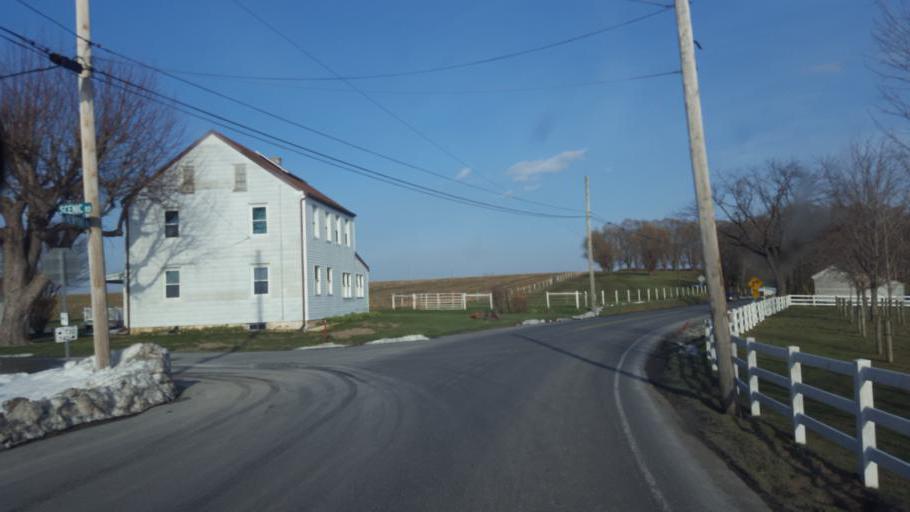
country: US
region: Pennsylvania
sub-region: Lancaster County
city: Intercourse
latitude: 40.0583
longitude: -76.1371
